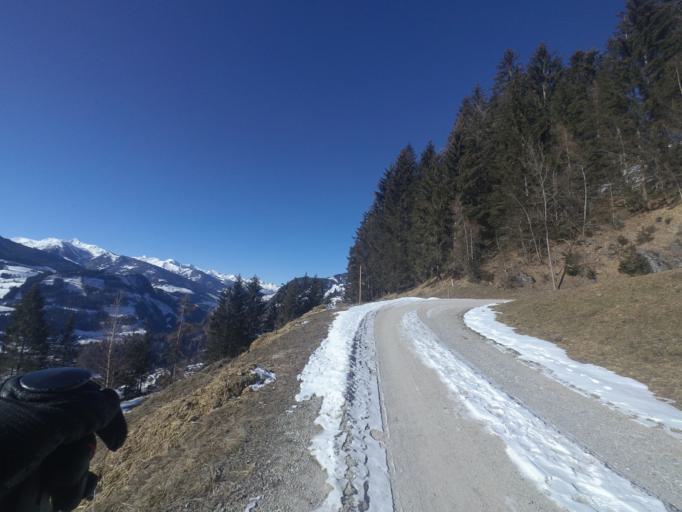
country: AT
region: Salzburg
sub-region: Politischer Bezirk Zell am See
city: Lend
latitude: 47.3173
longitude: 13.0433
